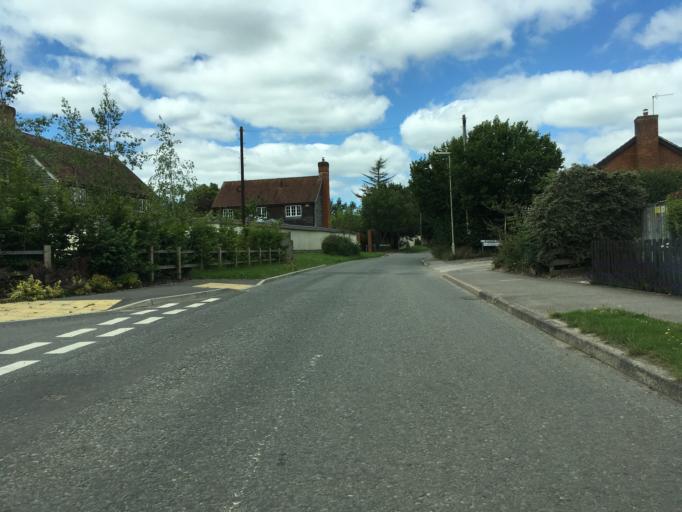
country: GB
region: England
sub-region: Hampshire
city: Overton
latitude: 51.2313
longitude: -1.3440
